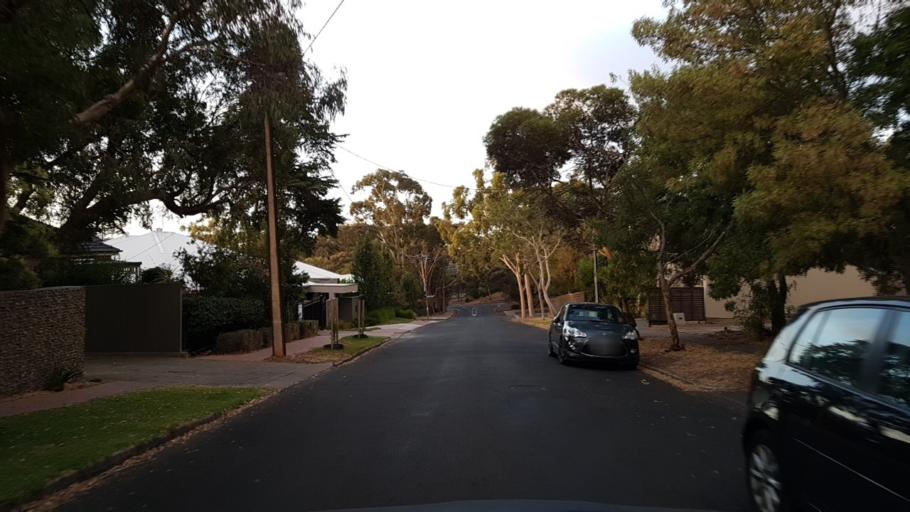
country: AU
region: South Australia
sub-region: Burnside
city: Hazelwood Park
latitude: -34.9402
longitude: 138.6684
